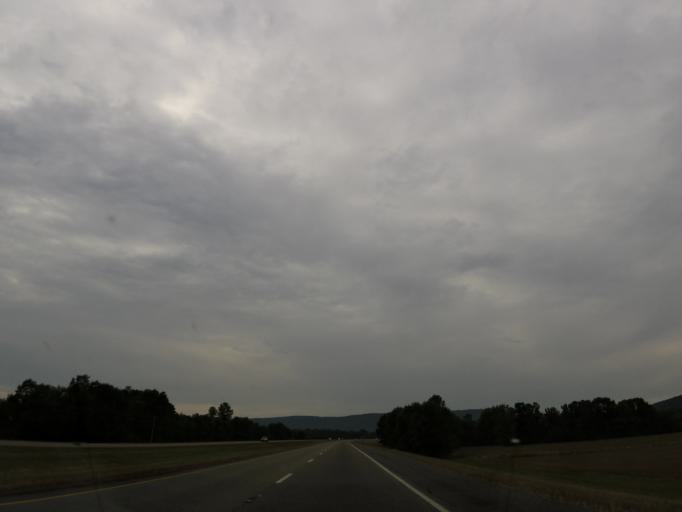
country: US
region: Alabama
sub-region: Madison County
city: New Hope
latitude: 34.6135
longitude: -86.2847
